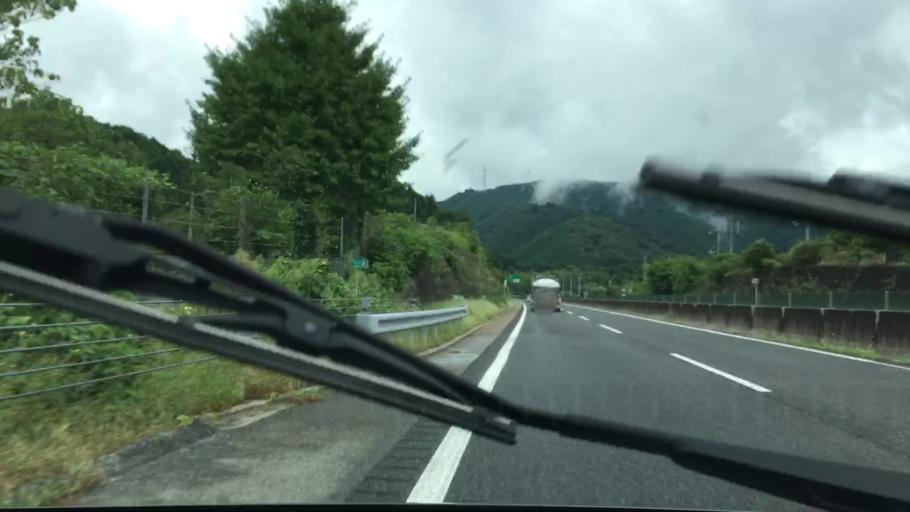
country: JP
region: Hyogo
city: Yamazakicho-nakabirose
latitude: 35.0271
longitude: 134.4903
